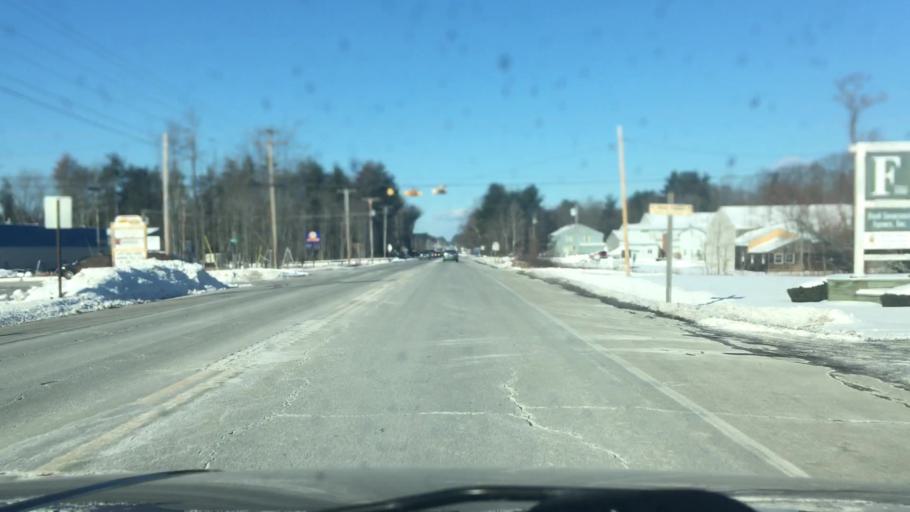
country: US
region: Maine
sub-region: York County
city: South Eliot
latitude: 43.1210
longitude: -70.7601
